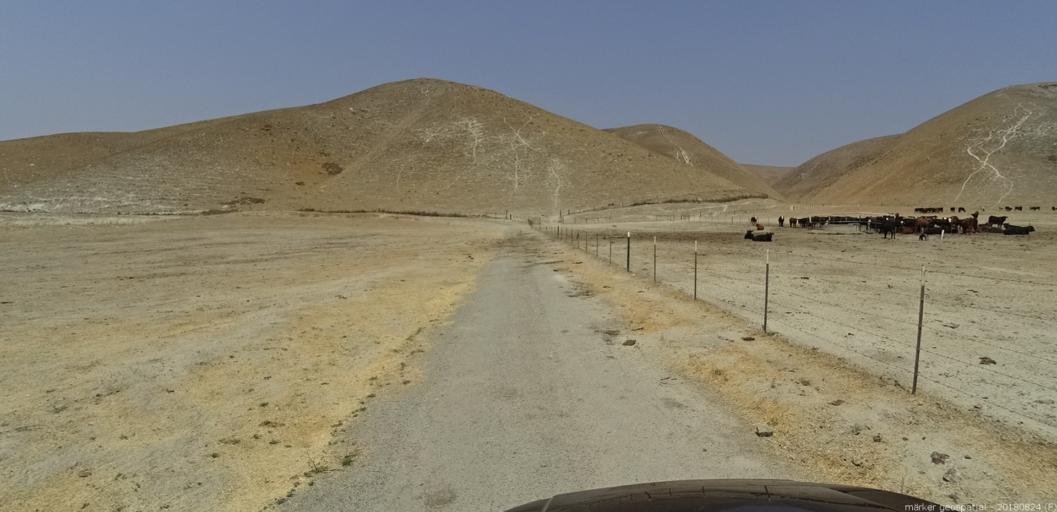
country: US
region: California
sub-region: Monterey County
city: King City
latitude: 36.2007
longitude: -120.9410
